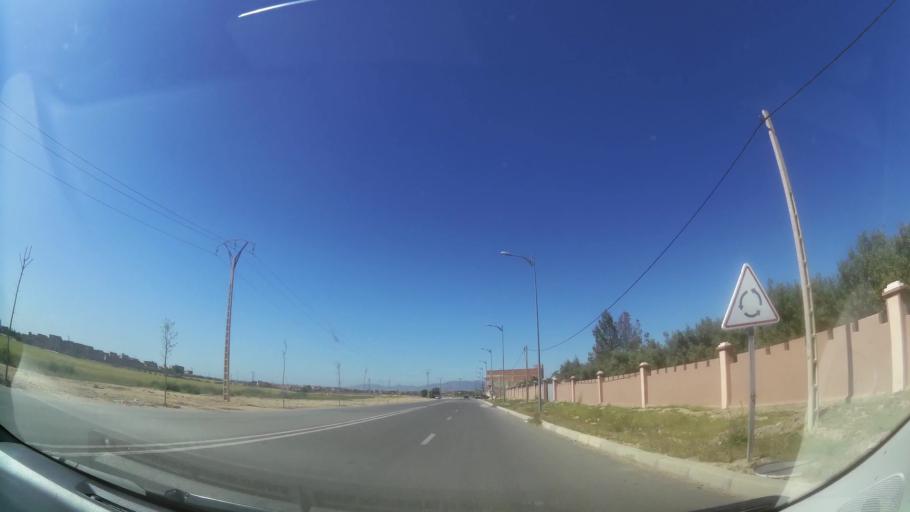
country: MA
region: Oriental
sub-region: Oujda-Angad
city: Oujda
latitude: 34.6939
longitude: -1.8568
